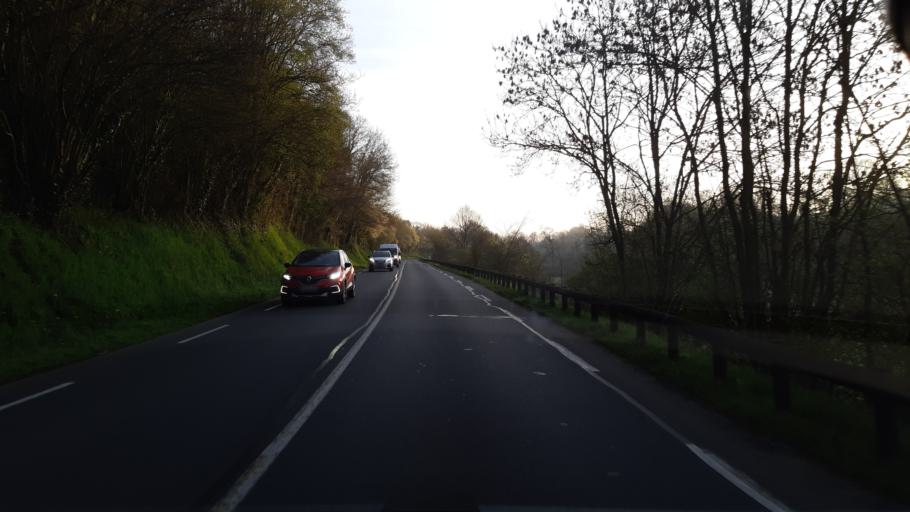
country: FR
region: Lower Normandy
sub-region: Departement de la Manche
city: Agneaux
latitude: 49.0753
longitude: -1.1266
